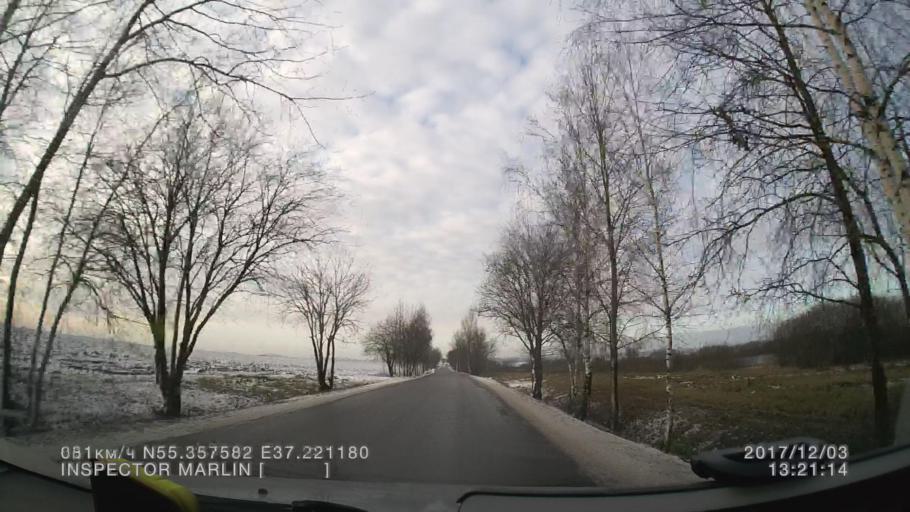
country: RU
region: Moskovskaya
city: Troitsk
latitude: 55.3576
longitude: 37.2213
